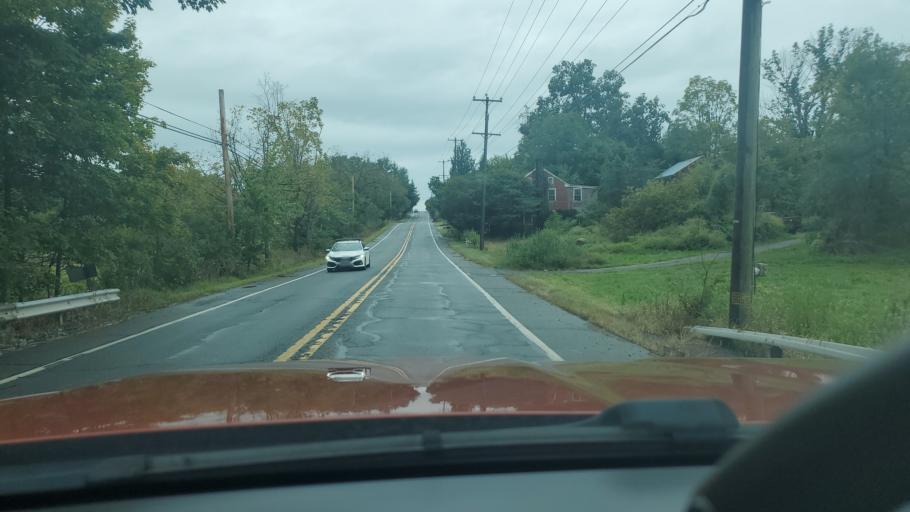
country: US
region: Pennsylvania
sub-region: Montgomery County
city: Spring Mount
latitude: 40.2867
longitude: -75.4813
